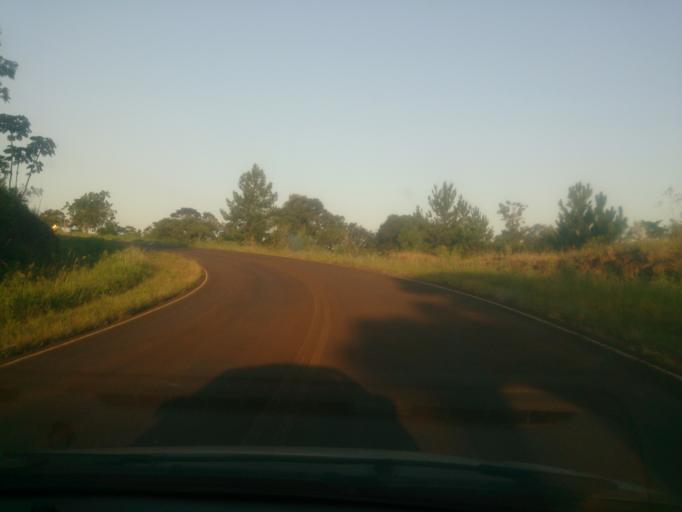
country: AR
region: Misiones
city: Panambi
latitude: -27.6642
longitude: -54.9127
